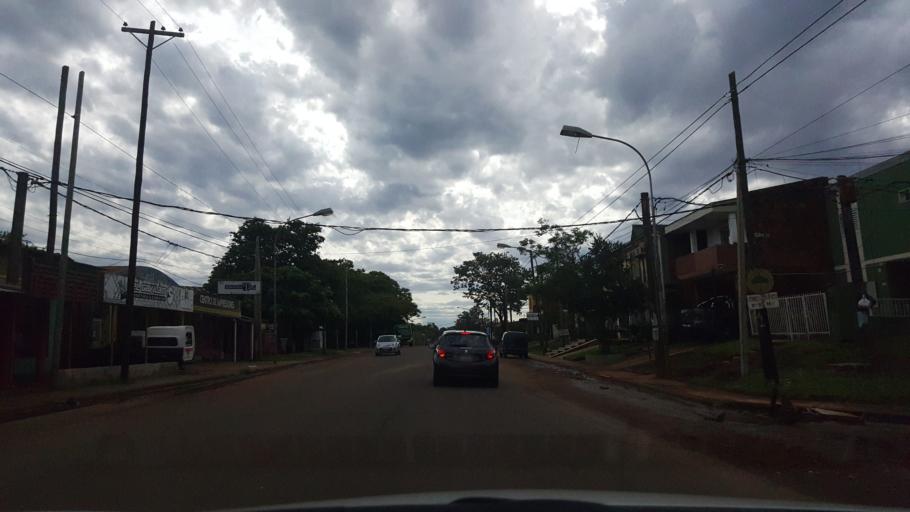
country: AR
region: Misiones
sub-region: Departamento de Capital
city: Posadas
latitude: -27.3704
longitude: -55.9336
